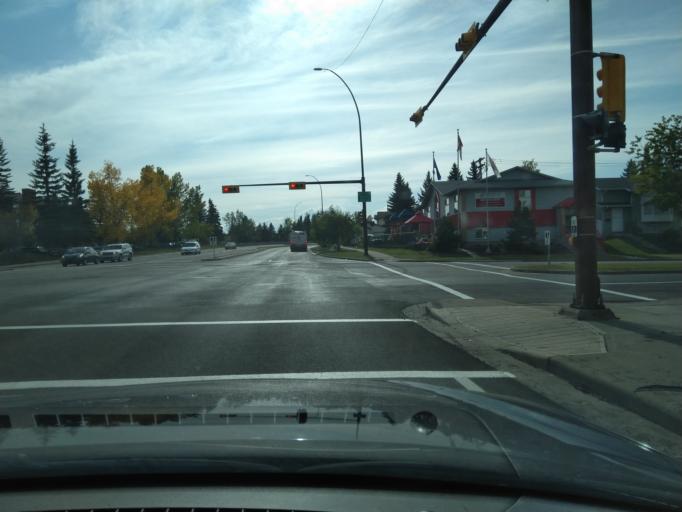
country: CA
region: Alberta
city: Calgary
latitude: 51.1264
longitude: -114.0553
